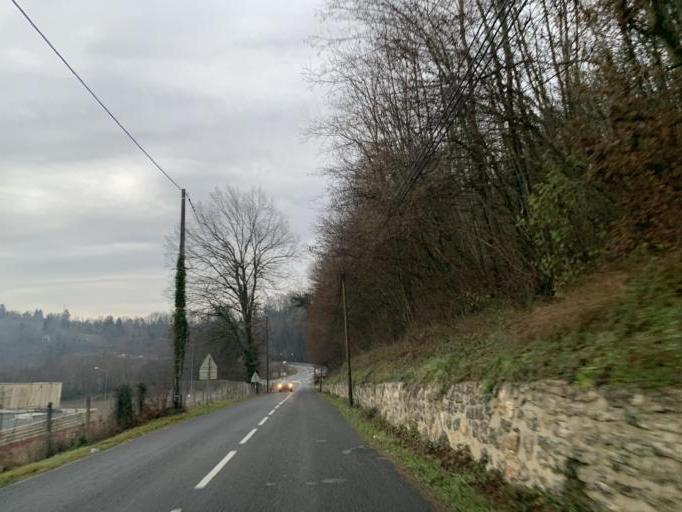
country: FR
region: Rhone-Alpes
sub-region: Departement de l'Ain
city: Belley
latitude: 45.7746
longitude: 5.6866
